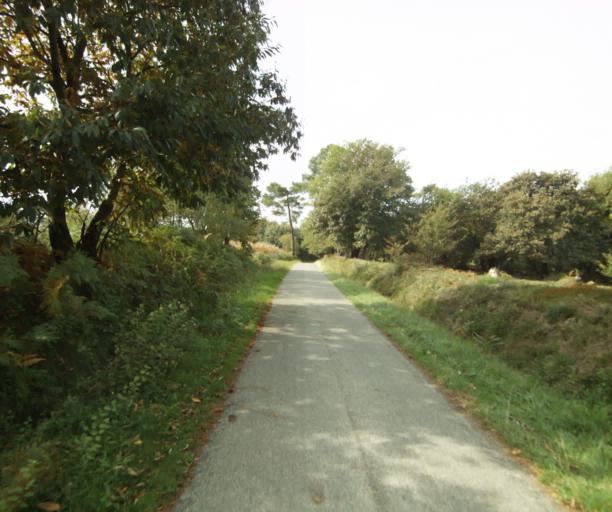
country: FR
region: Midi-Pyrenees
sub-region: Departement du Gers
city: Eauze
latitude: 43.8192
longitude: 0.1301
